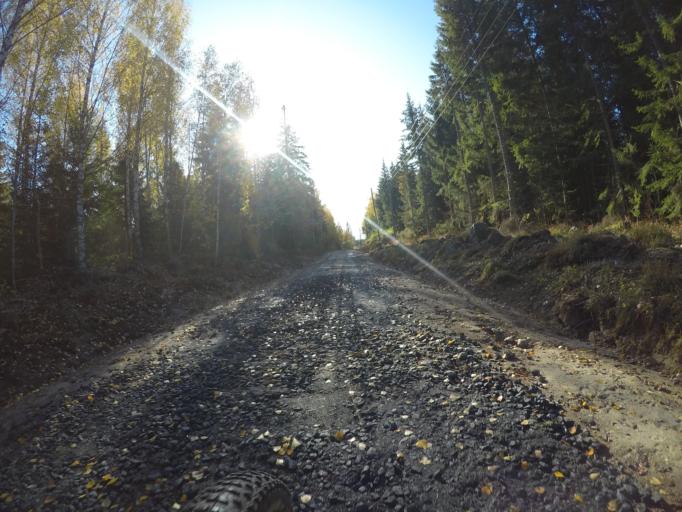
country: SE
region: Vaestmanland
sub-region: Kungsors Kommun
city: Kungsoer
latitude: 59.3132
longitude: 16.0978
